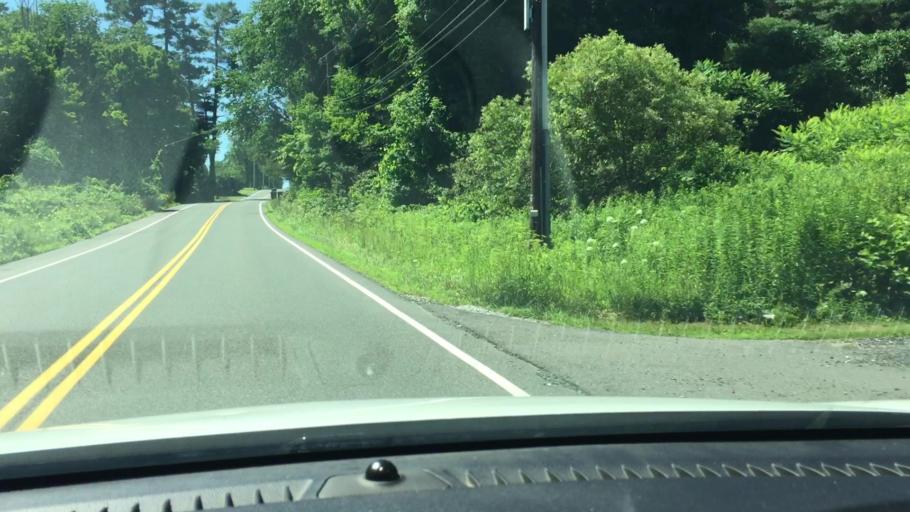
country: US
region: Massachusetts
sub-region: Berkshire County
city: Lenox
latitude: 42.3633
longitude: -73.2596
